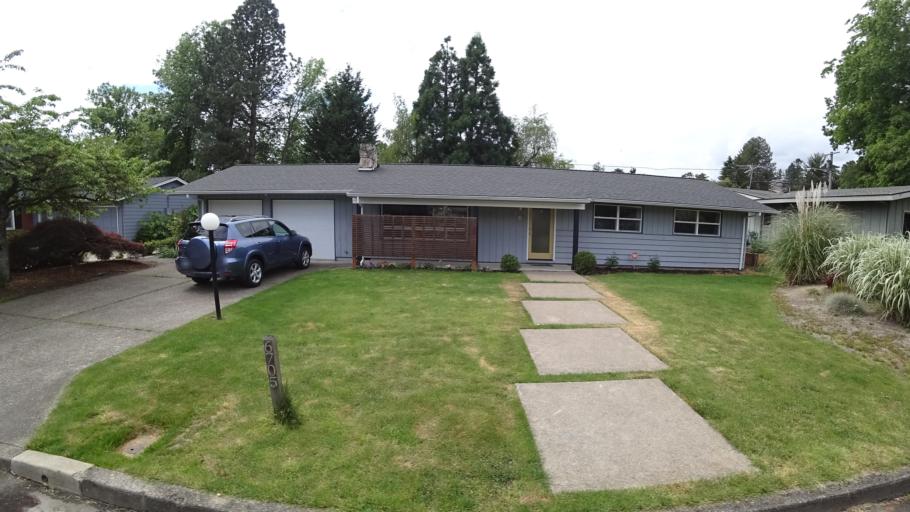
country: US
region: Oregon
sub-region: Washington County
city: Raleigh Hills
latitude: 45.4714
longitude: -122.7697
